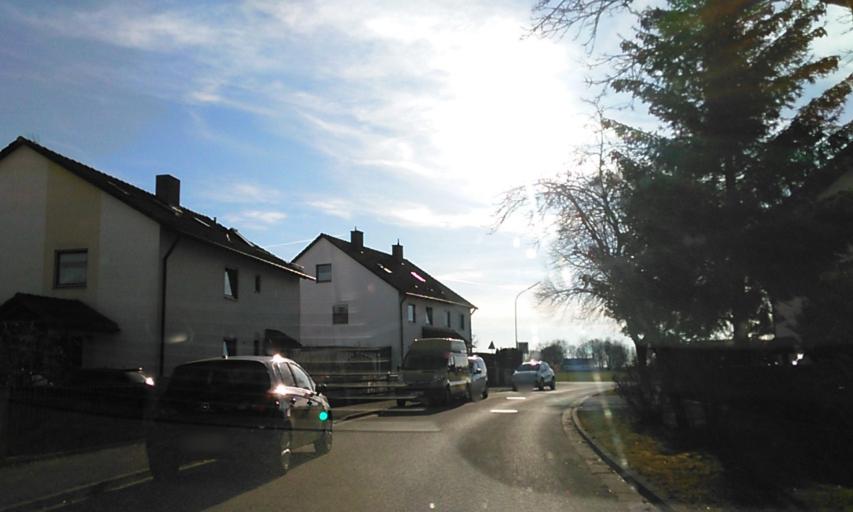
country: DE
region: Bavaria
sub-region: Swabia
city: Merching
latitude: 48.2408
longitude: 10.9912
